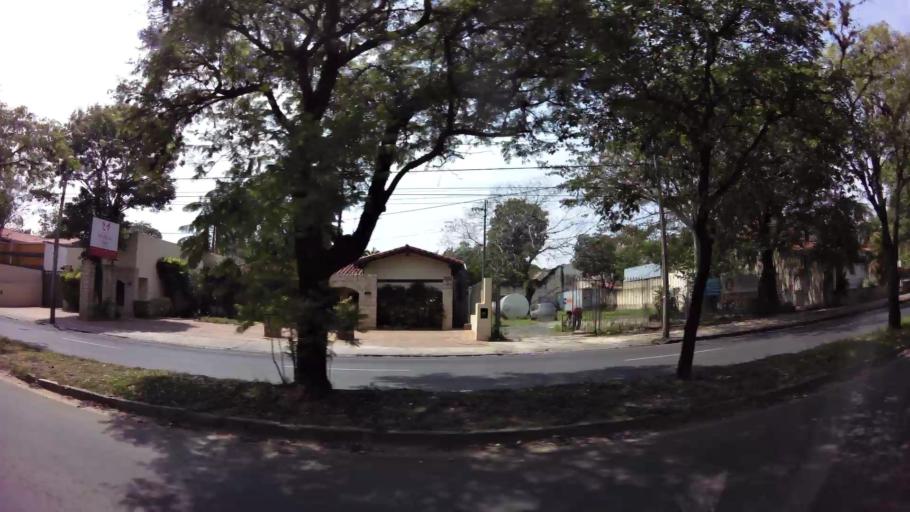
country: PY
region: Asuncion
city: Asuncion
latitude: -25.2836
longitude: -57.5879
